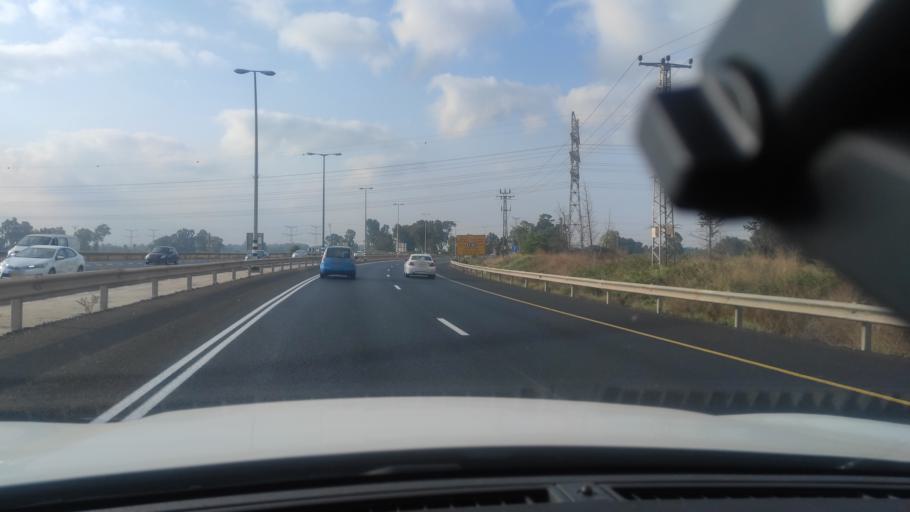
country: IL
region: Central District
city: Hod HaSharon
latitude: 32.1285
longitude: 34.9030
